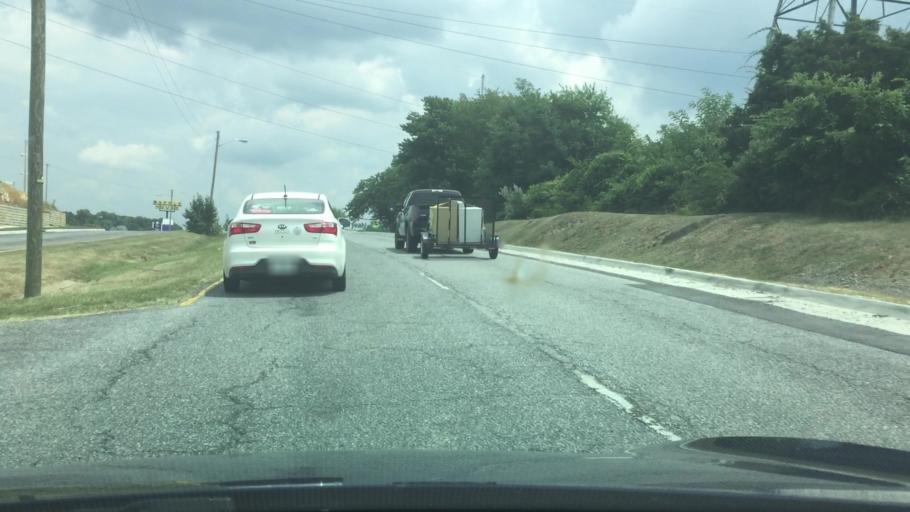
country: US
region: Virginia
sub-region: Wythe County
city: Wytheville
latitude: 36.9477
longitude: -81.0609
